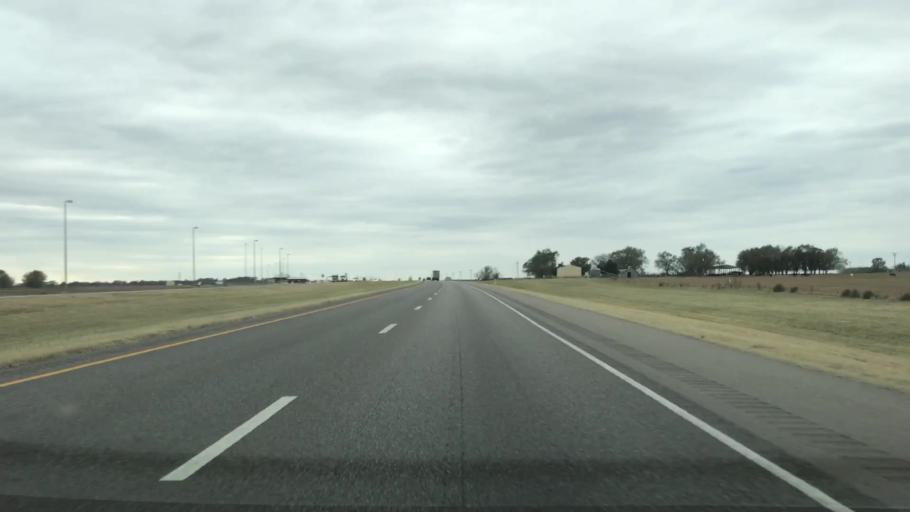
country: US
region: Oklahoma
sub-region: Beckham County
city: Erick
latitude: 35.2320
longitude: -99.9601
